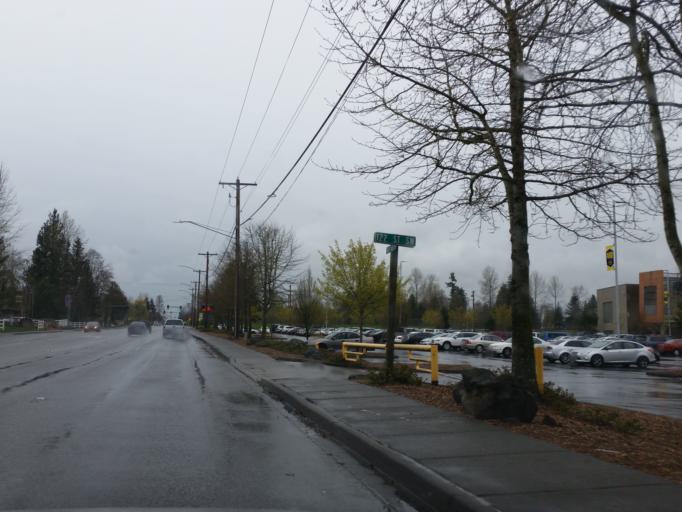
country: US
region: Washington
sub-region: Snohomish County
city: Martha Lake
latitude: 47.8873
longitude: -122.2388
